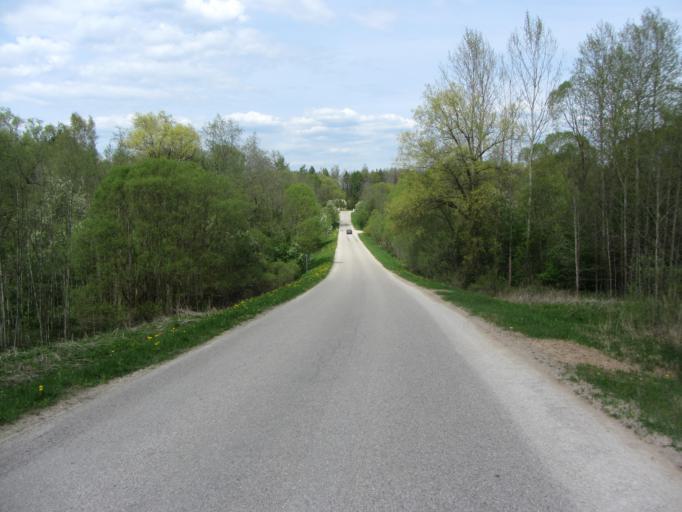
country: LT
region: Utenos apskritis
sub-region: Anyksciai
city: Anyksciai
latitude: 55.4189
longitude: 25.1109
